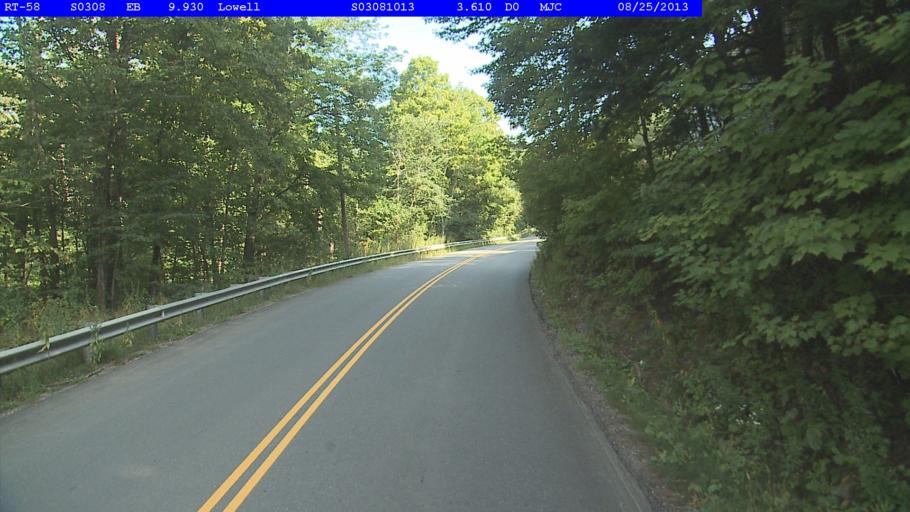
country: US
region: Vermont
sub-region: Lamoille County
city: Hyde Park
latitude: 44.8034
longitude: -72.4563
